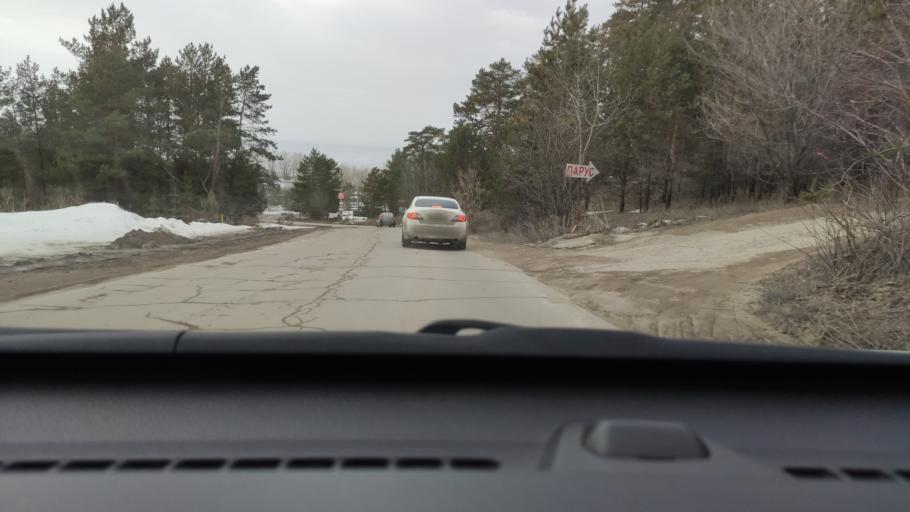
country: RU
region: Samara
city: Tol'yatti
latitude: 53.4722
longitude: 49.3705
